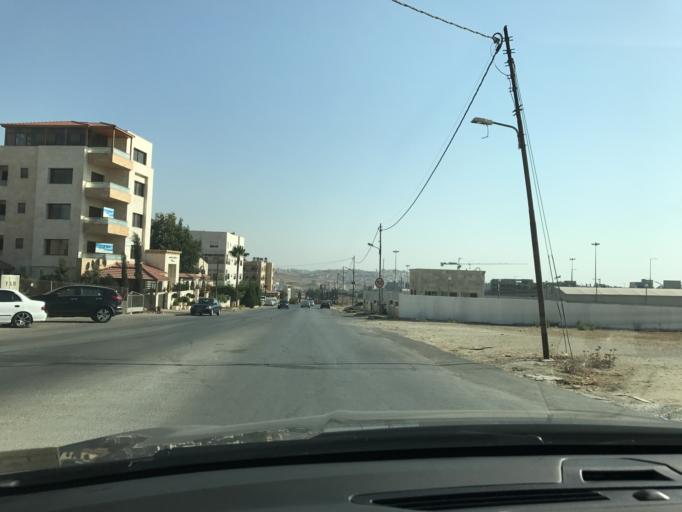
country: JO
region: Amman
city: Wadi as Sir
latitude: 31.9477
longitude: 35.8516
